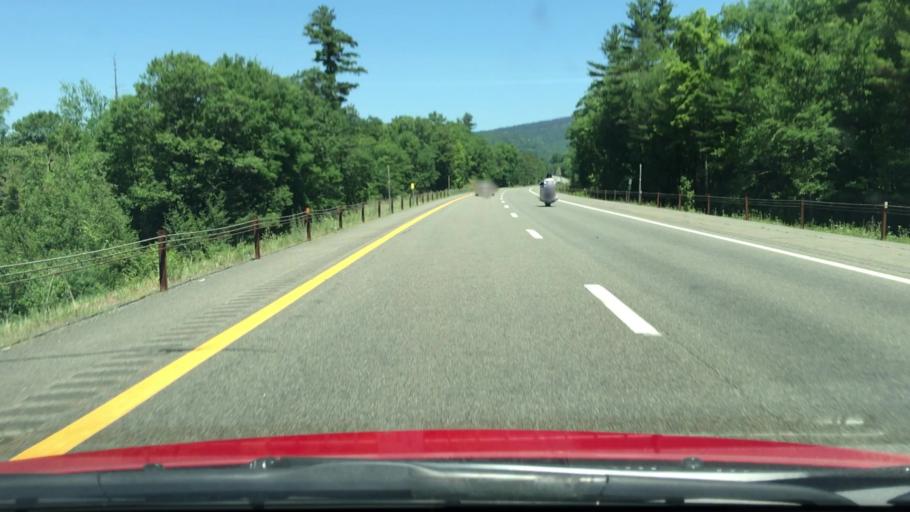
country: US
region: New York
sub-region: Essex County
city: Elizabethtown
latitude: 44.3528
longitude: -73.5330
